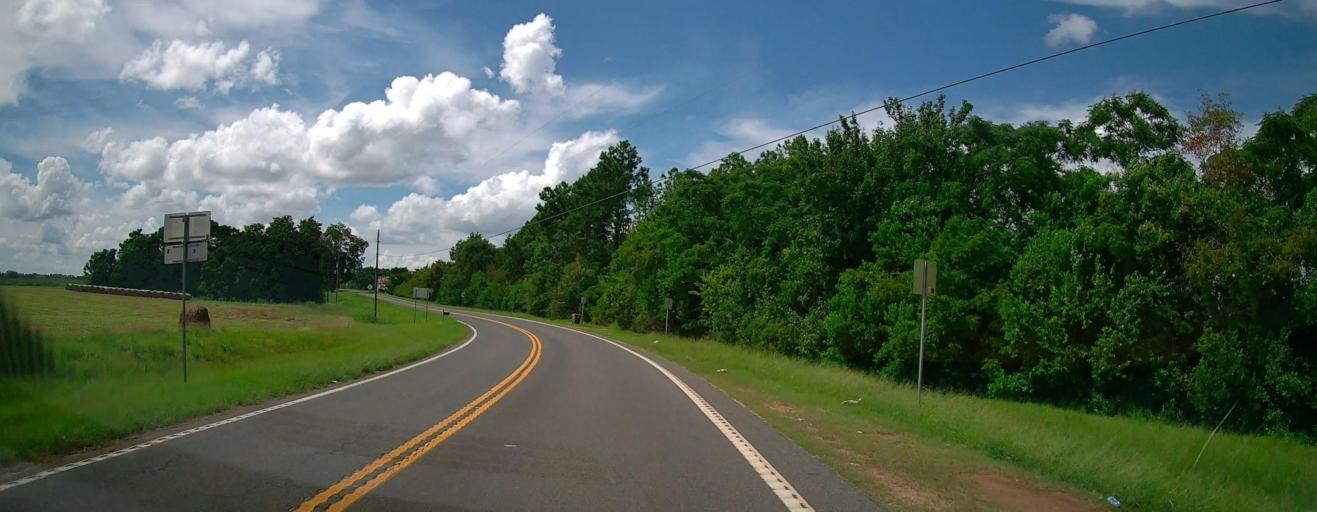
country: US
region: Georgia
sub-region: Macon County
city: Marshallville
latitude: 32.4324
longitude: -84.0033
